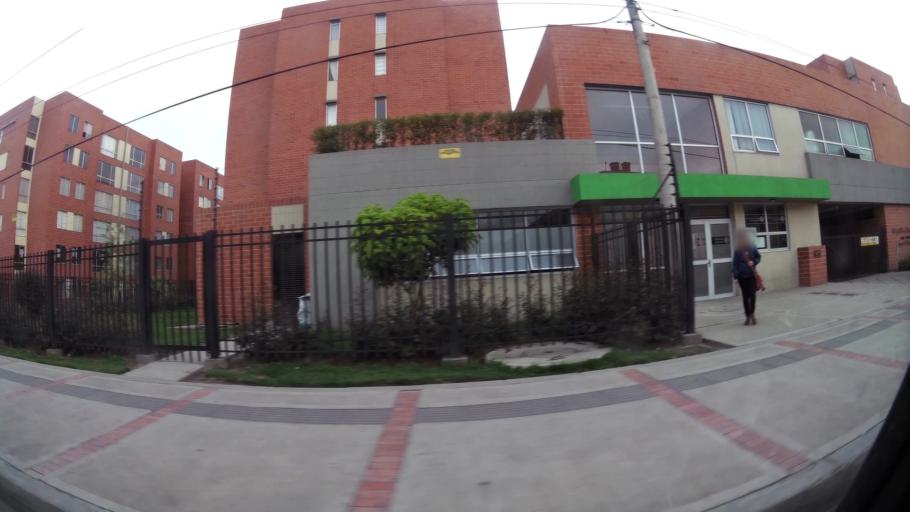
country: CO
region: Cundinamarca
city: Mosquera
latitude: 4.7113
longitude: -74.2294
